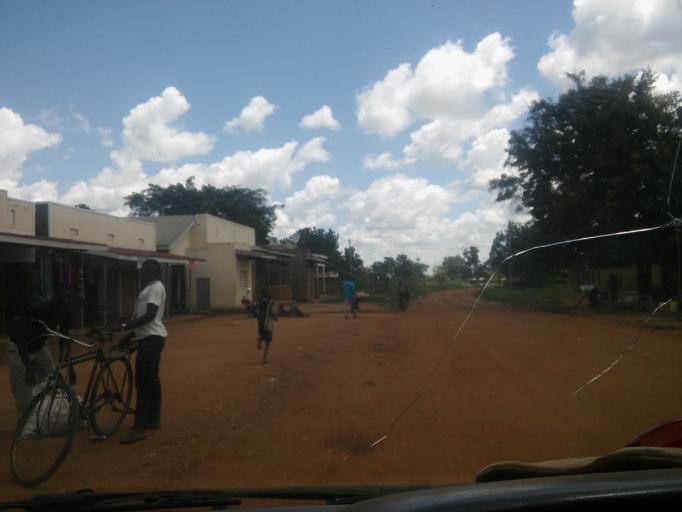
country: UG
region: Eastern Region
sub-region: Mbale District
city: Mbale
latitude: 1.0763
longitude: 34.0946
